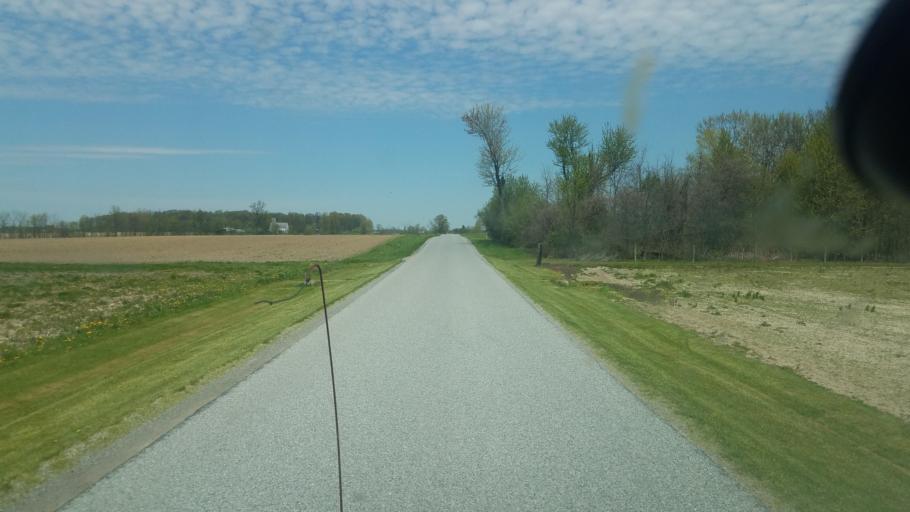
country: US
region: Ohio
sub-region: Hardin County
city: Ada
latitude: 40.8046
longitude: -83.8990
